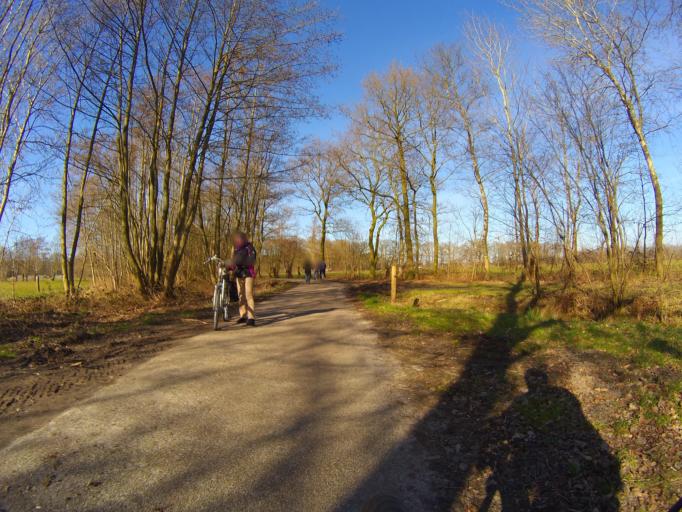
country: NL
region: Utrecht
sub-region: Gemeente Utrechtse Heuvelrug
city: Overberg
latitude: 52.0672
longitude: 5.4927
